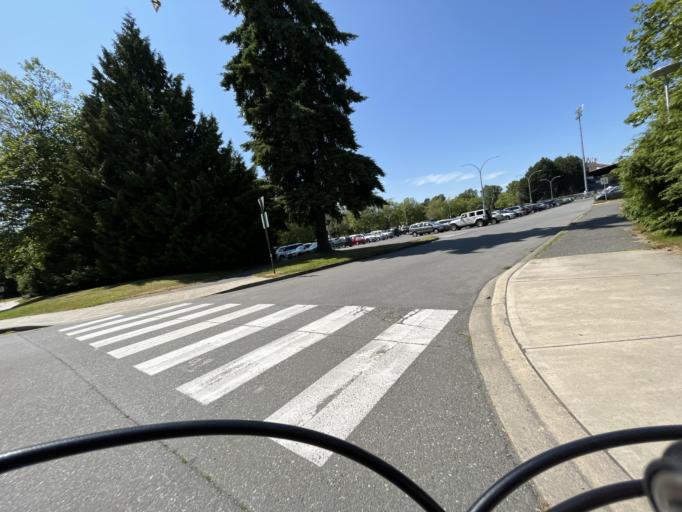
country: CA
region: British Columbia
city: Oak Bay
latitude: 48.4656
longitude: -123.3144
